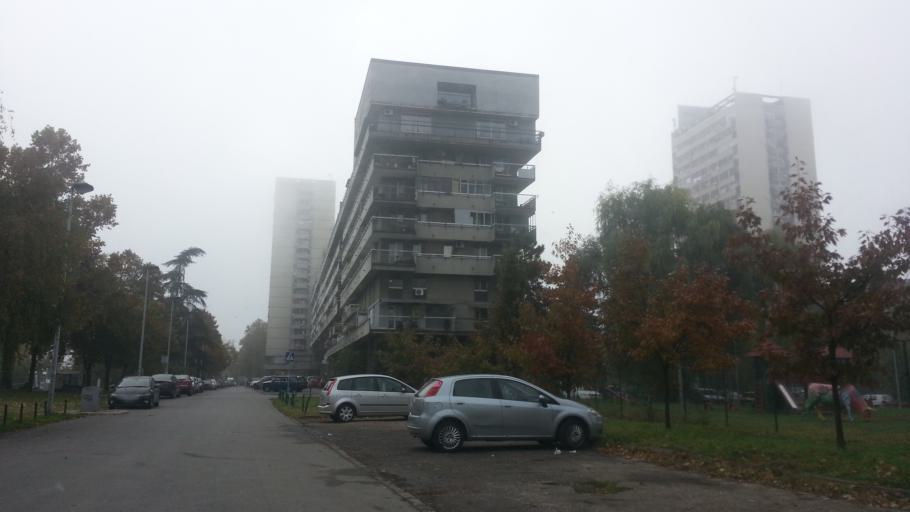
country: RS
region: Central Serbia
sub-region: Belgrade
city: Zemun
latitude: 44.8393
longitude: 20.4183
